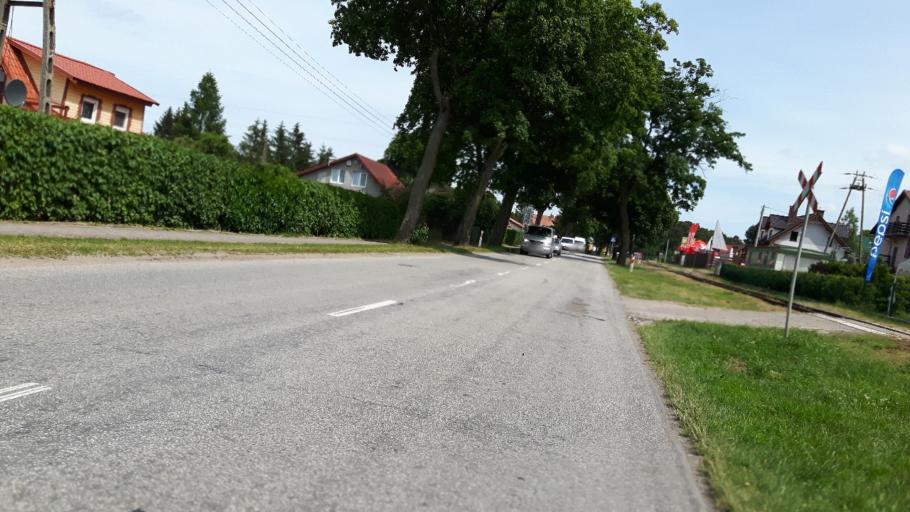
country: PL
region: Pomeranian Voivodeship
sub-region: Powiat nowodworski
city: Stegna
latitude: 54.3333
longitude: 19.0429
